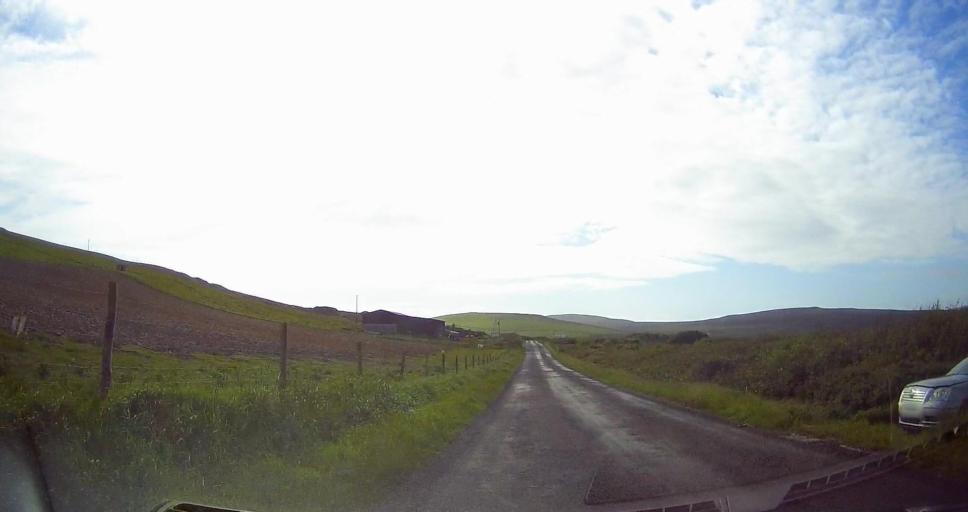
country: GB
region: Scotland
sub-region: Orkney Islands
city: Stromness
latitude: 58.7844
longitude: -3.2415
